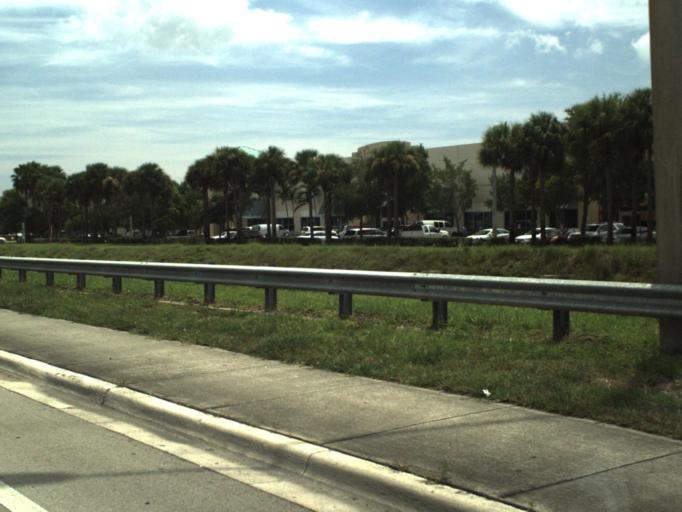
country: US
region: Florida
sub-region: Broward County
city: Pompano Beach
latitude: 26.2313
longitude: -80.1489
